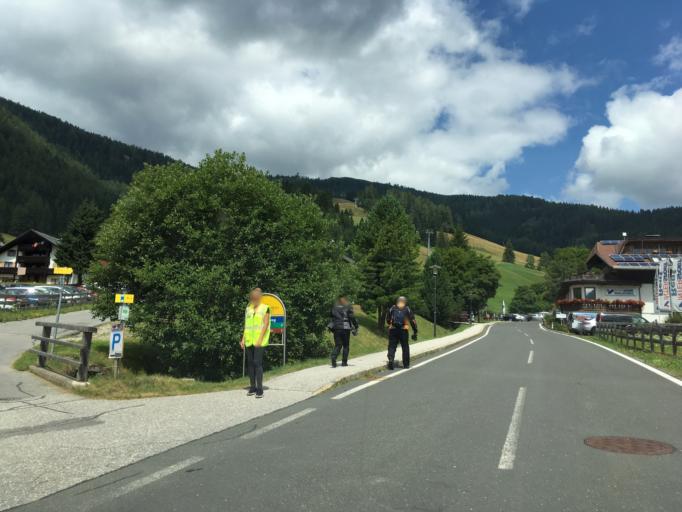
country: AT
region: Carinthia
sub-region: Politischer Bezirk Spittal an der Drau
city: Kleinkirchheim
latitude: 46.8434
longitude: 13.7649
